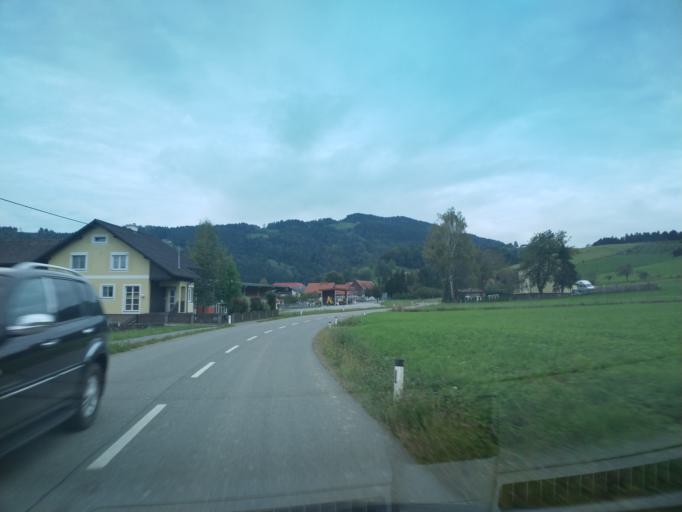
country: AT
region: Styria
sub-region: Politischer Bezirk Deutschlandsberg
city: Wernersdorf
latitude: 46.7166
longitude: 15.2113
